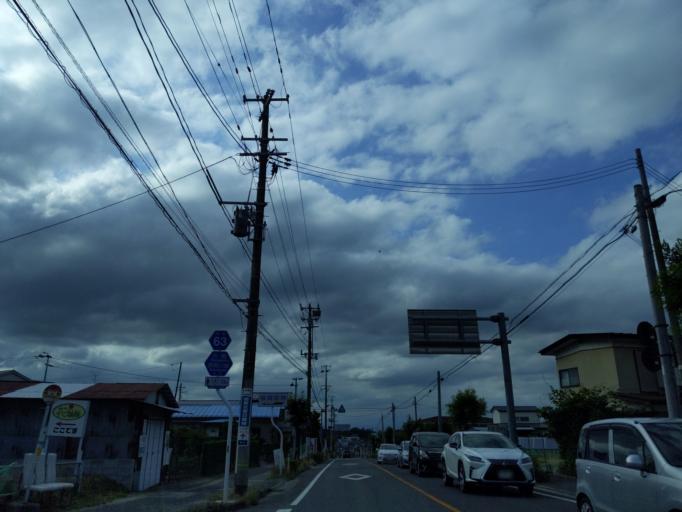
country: JP
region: Fukushima
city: Sukagawa
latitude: 37.2798
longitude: 140.3850
